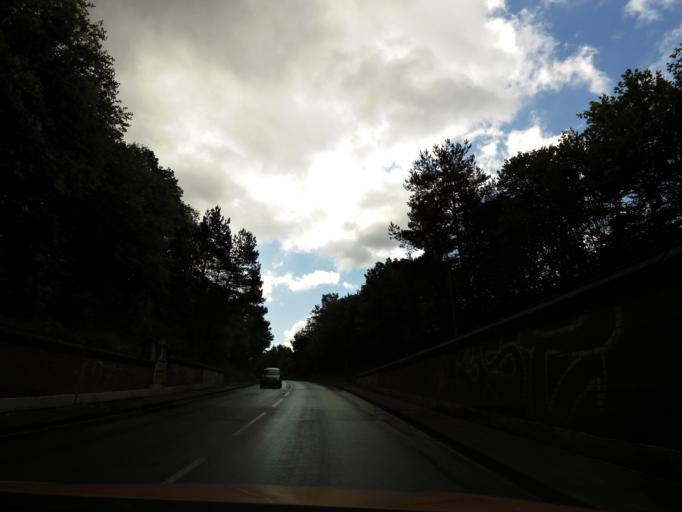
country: DE
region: Lower Saxony
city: Hude
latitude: 53.1033
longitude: 8.4762
